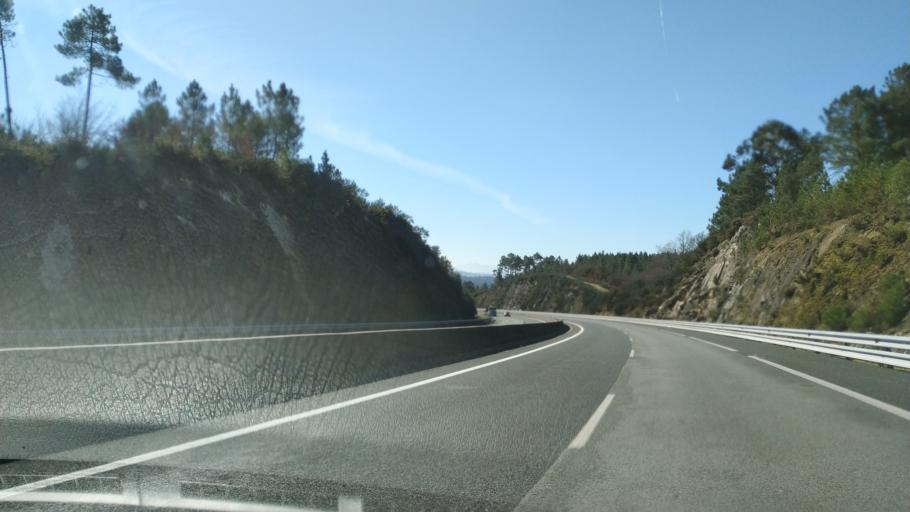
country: ES
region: Galicia
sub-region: Provincia de Ourense
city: Pinor
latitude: 42.5021
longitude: -8.0274
